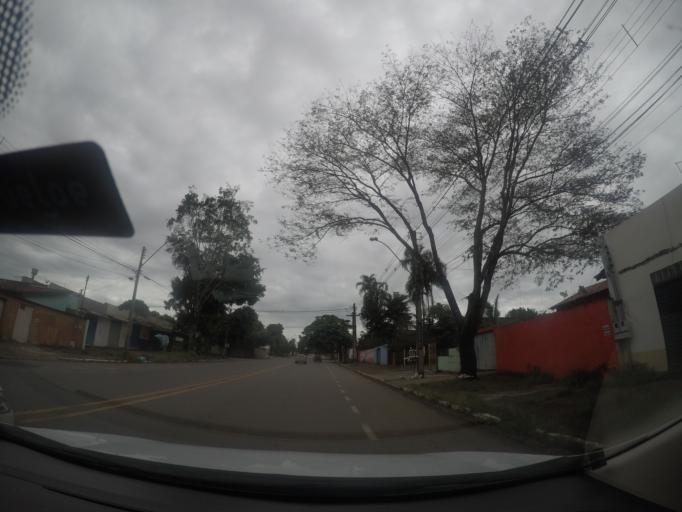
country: BR
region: Goias
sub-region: Goiania
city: Goiania
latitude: -16.6085
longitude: -49.2950
